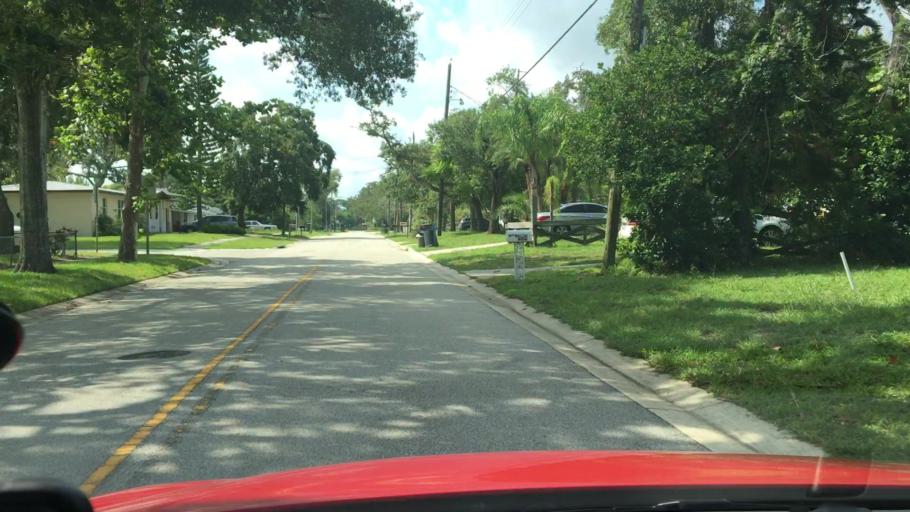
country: US
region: Florida
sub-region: Volusia County
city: Ormond Beach
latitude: 29.2711
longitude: -81.0520
